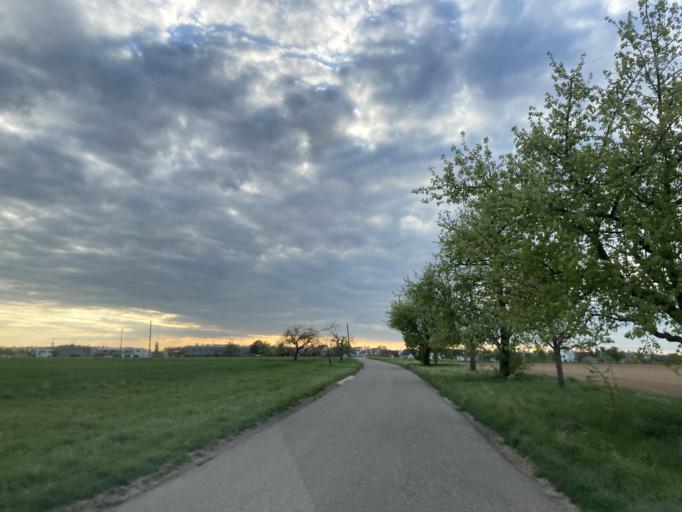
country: DE
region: Baden-Wuerttemberg
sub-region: Tuebingen Region
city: Kusterdingen
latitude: 48.5174
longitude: 9.1296
